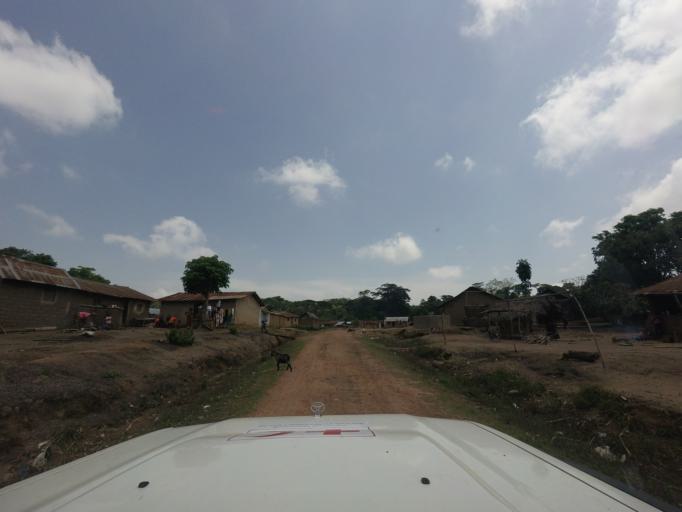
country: LR
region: Lofa
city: Voinjama
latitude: 8.4868
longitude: -9.6625
